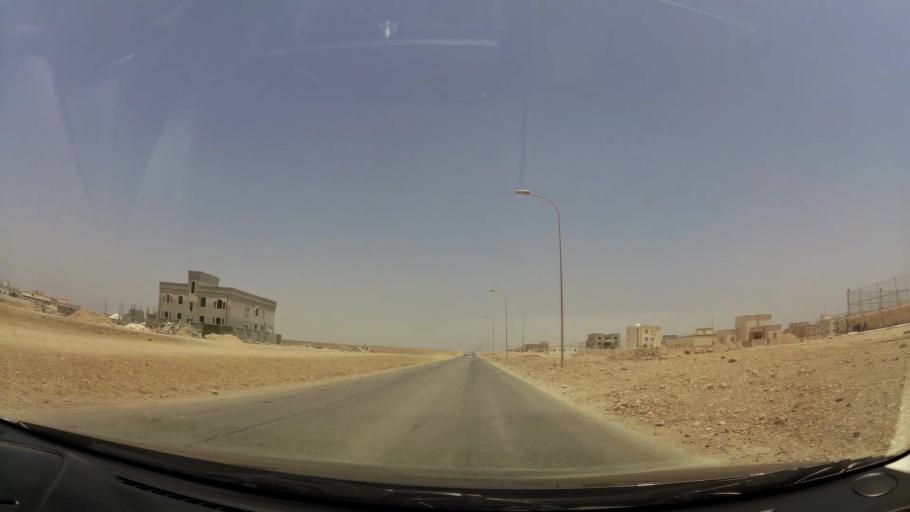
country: OM
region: Zufar
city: Salalah
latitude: 17.0916
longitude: 54.1846
